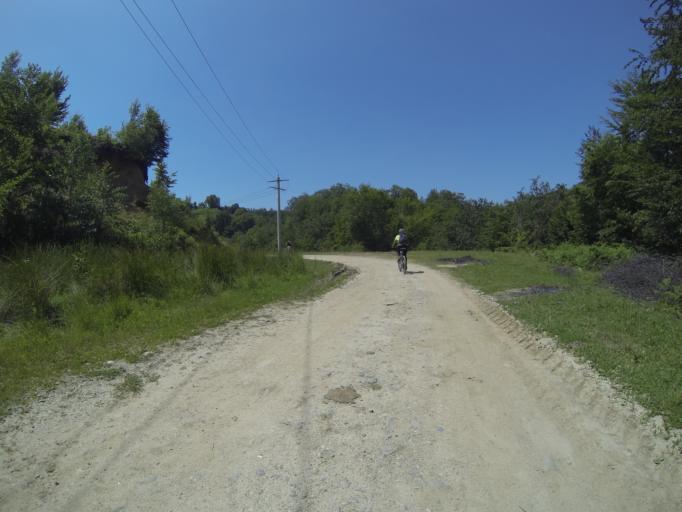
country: RO
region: Valcea
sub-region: Oras Baile Olanesti
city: Baile Olanesti
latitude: 45.2076
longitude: 24.2160
